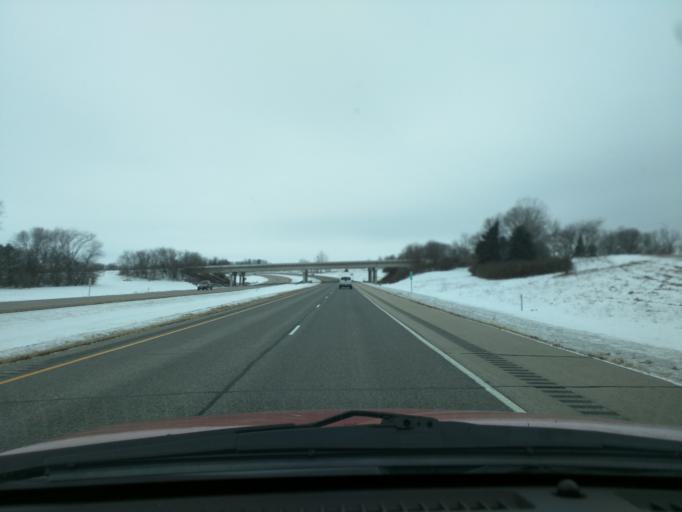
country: US
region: Minnesota
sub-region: Winona County
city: Winona
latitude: 43.9567
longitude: -91.6832
